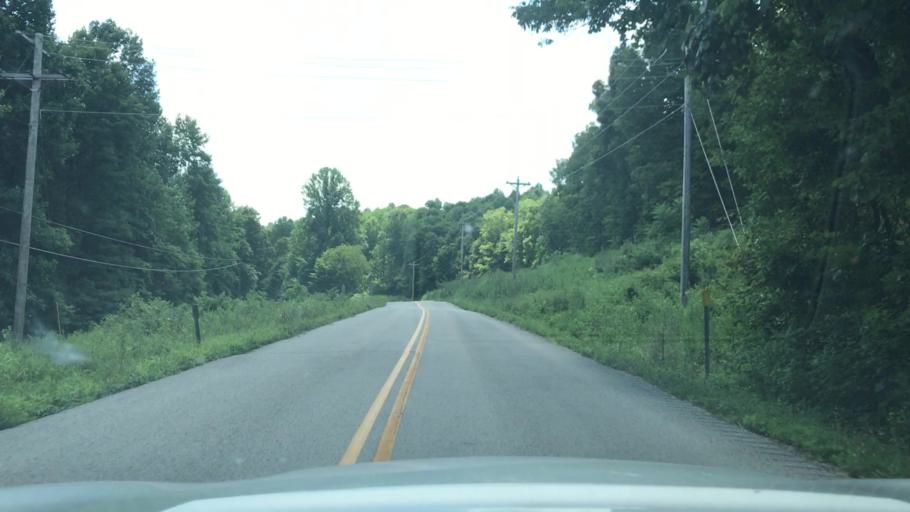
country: US
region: Kentucky
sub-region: Hopkins County
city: Nortonville
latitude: 37.0459
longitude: -87.3469
